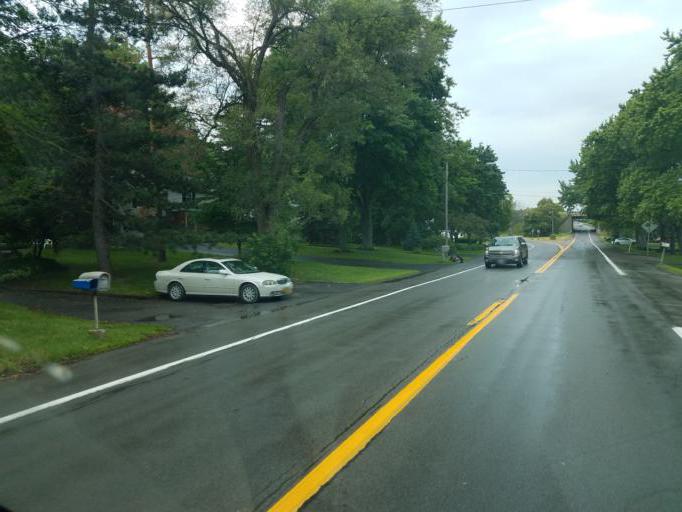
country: US
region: New York
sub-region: Niagara County
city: Lewiston
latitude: 43.1690
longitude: -79.0273
